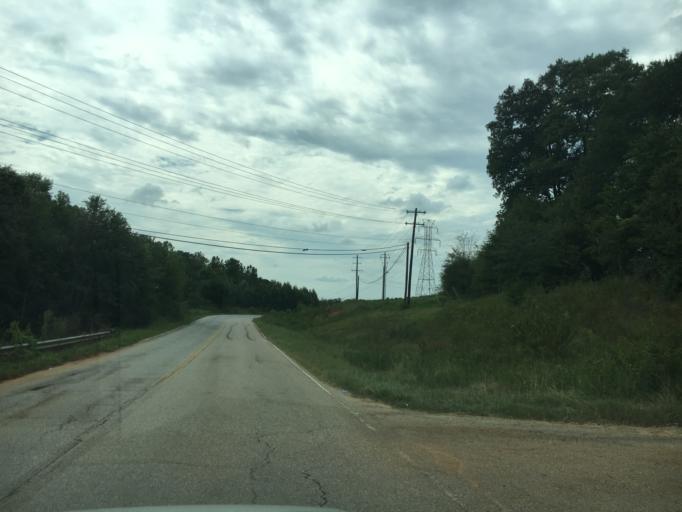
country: US
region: South Carolina
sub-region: Greenville County
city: Greer
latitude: 34.9256
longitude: -82.1919
